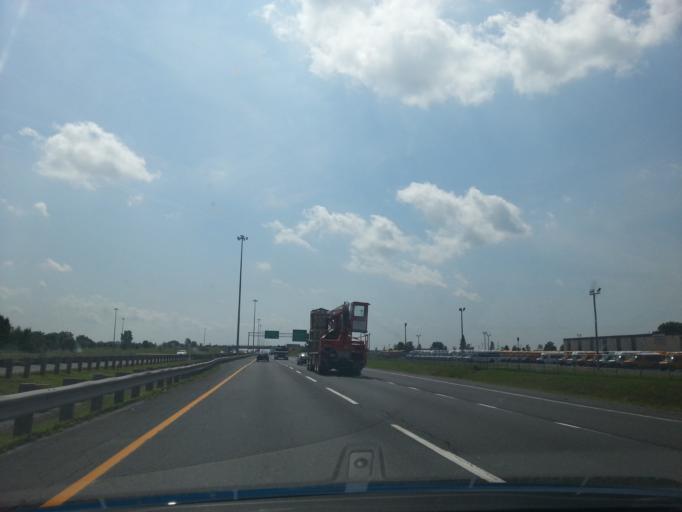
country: CA
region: Quebec
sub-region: Centre-du-Quebec
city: Drummondville
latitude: 45.9056
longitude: -72.5213
